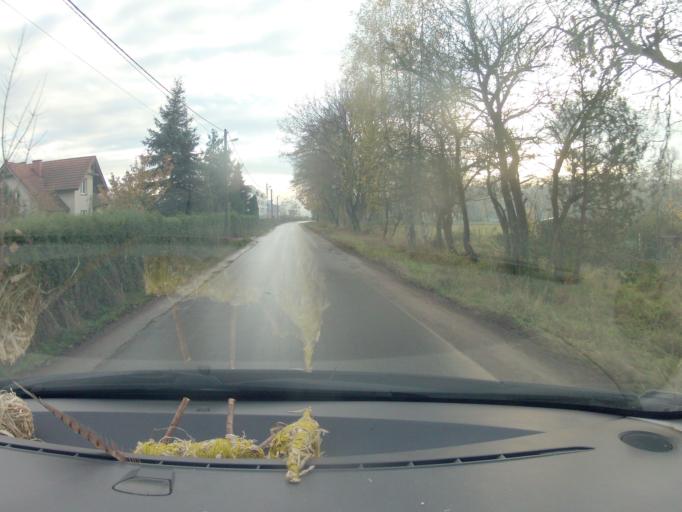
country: PL
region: Lesser Poland Voivodeship
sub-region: Krakow
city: Sidzina
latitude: 50.0037
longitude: 19.8892
